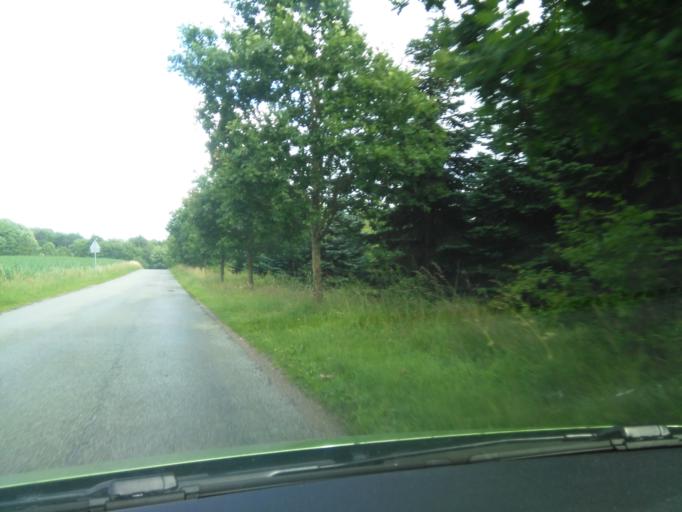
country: DK
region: Central Jutland
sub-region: Horsens Kommune
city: Braedstrup
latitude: 55.9756
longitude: 9.6917
